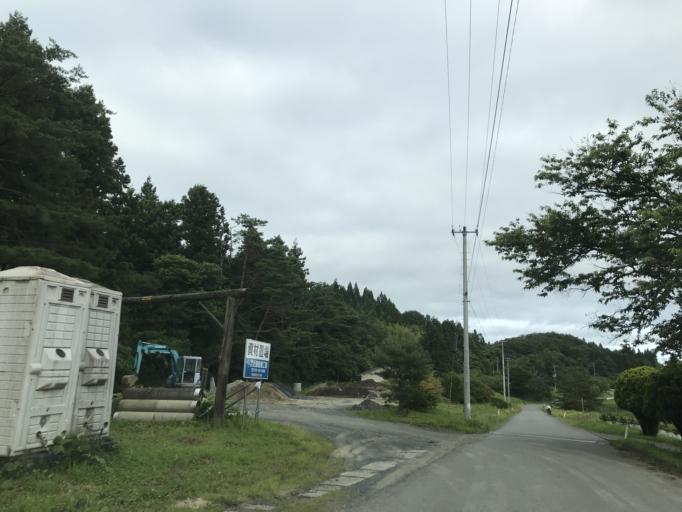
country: JP
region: Iwate
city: Ichinoseki
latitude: 38.8265
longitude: 141.2300
